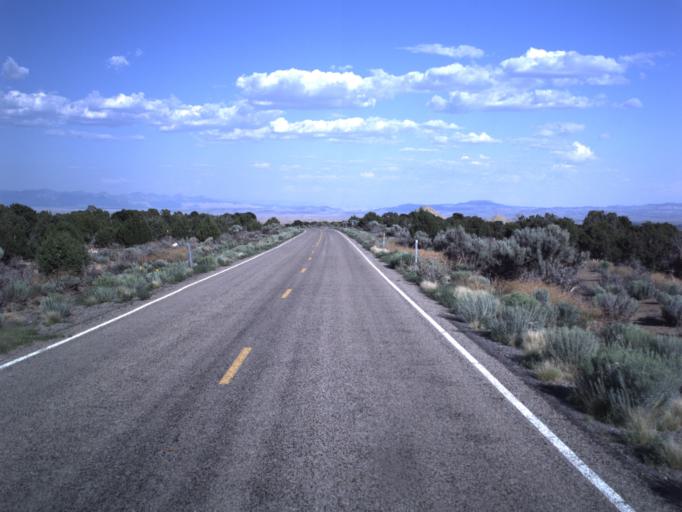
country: US
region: Utah
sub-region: Emery County
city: Huntington
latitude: 39.4859
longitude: -110.9347
